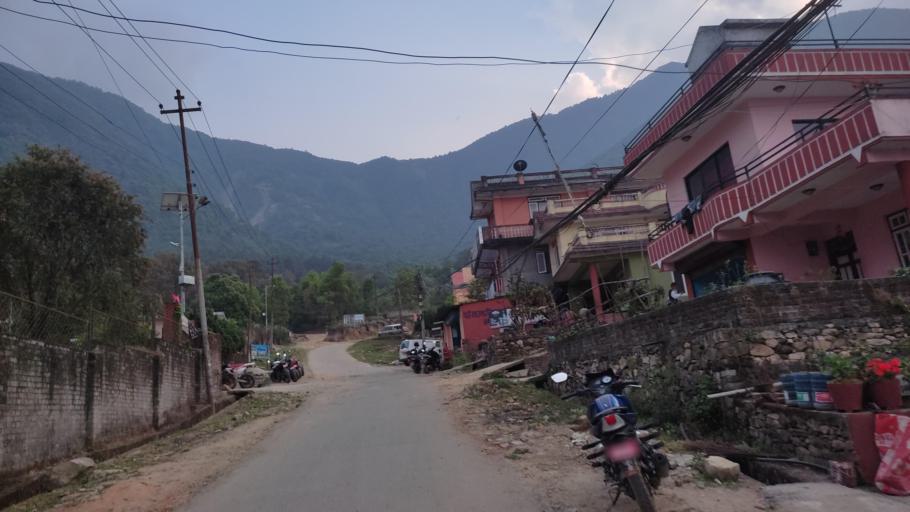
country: NP
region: Central Region
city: Kirtipur
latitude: 27.6587
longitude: 85.2512
